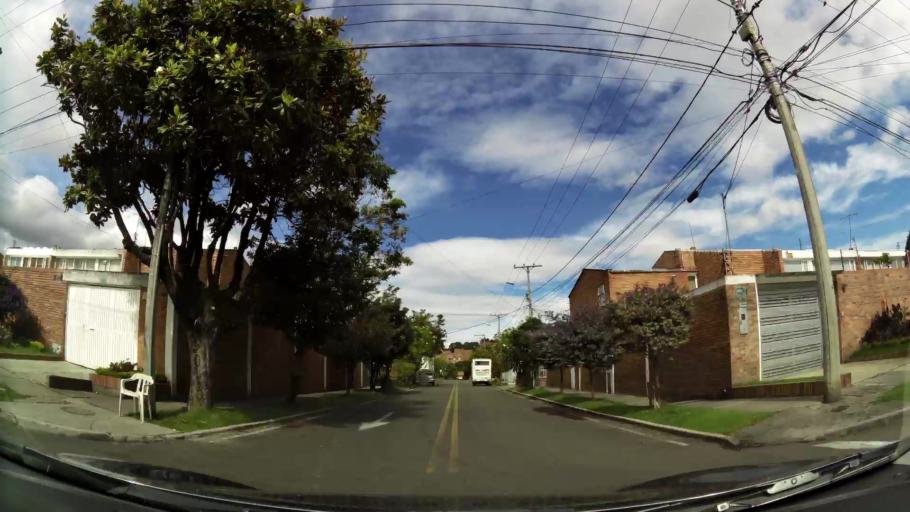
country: CO
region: Bogota D.C.
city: Barrio San Luis
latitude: 4.7083
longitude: -74.0759
